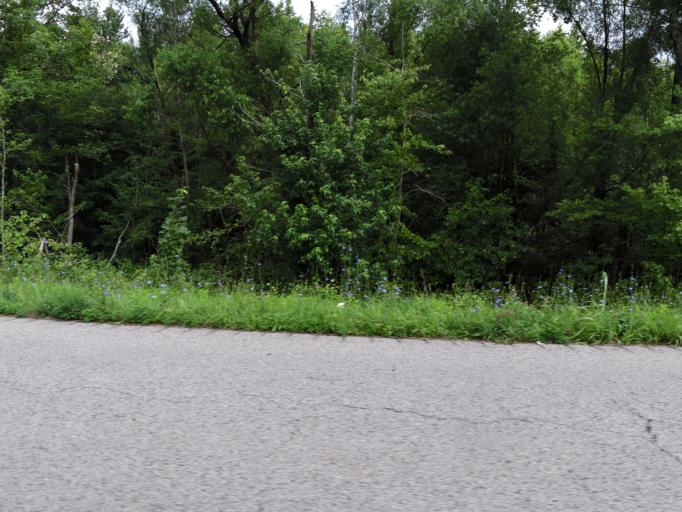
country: US
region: Kentucky
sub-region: Muhlenberg County
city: Morehead
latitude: 37.3025
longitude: -87.3252
